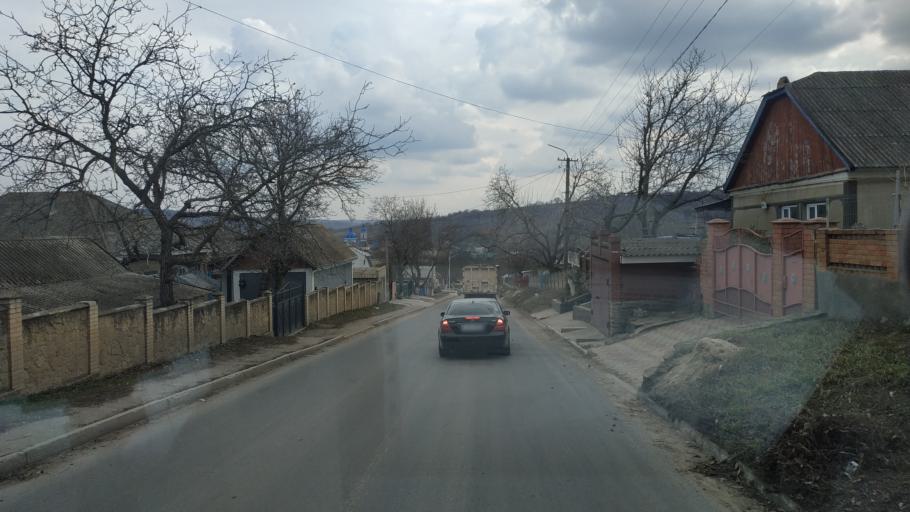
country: MD
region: Anenii Noi
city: Varnita
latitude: 46.8464
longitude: 29.3566
